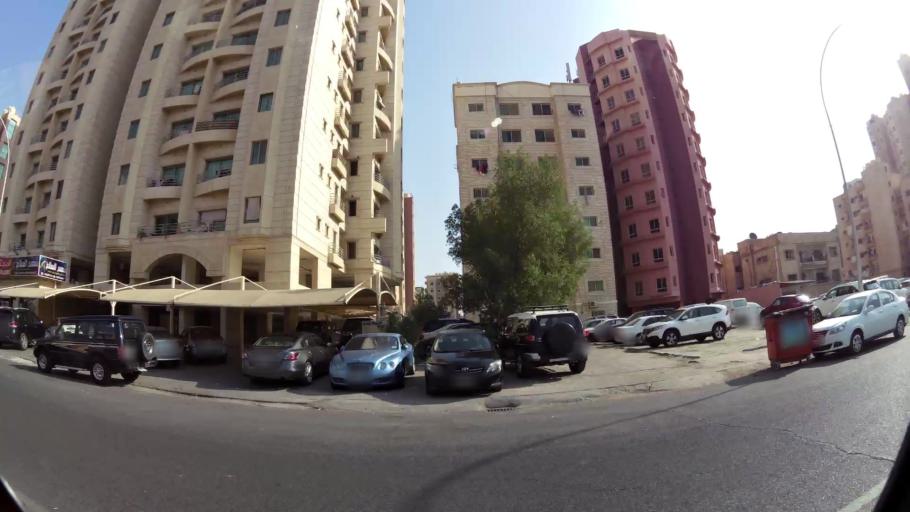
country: KW
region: Muhafazat Hawalli
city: Hawalli
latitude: 29.3268
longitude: 48.0130
